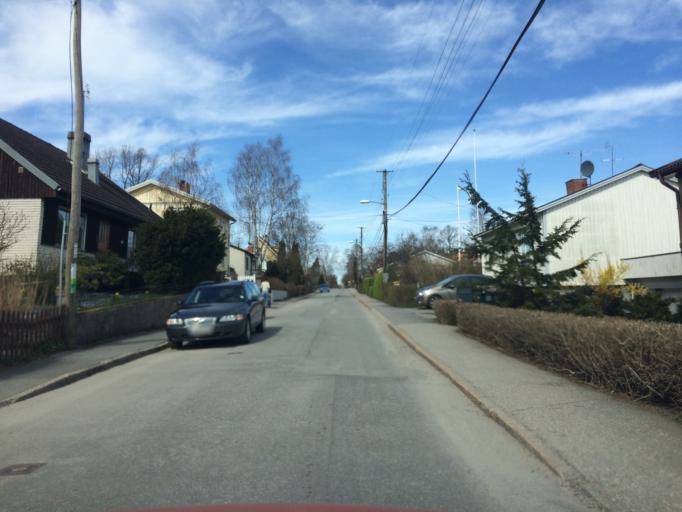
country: SE
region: Stockholm
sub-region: Huddinge Kommun
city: Huddinge
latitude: 59.2792
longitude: 17.9873
